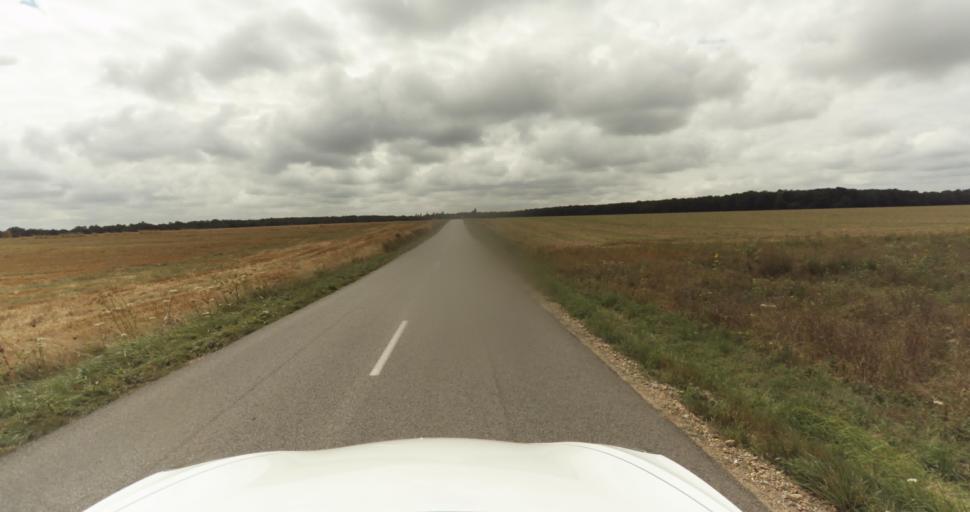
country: FR
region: Haute-Normandie
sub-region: Departement de l'Eure
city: Claville
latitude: 49.0131
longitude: 1.0340
